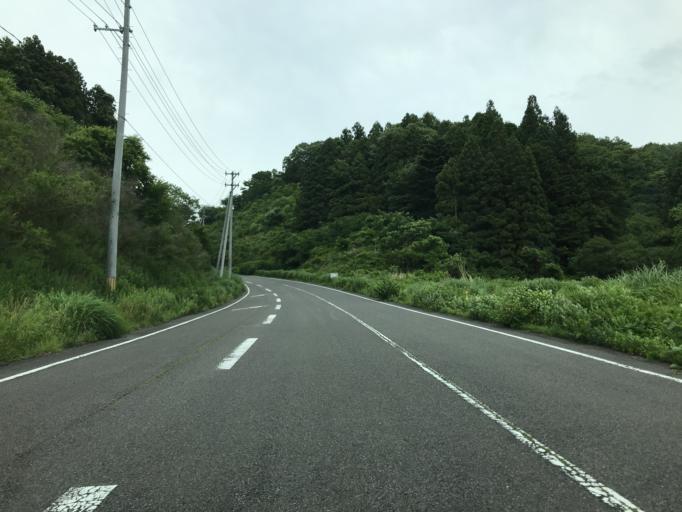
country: JP
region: Fukushima
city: Funehikimachi-funehiki
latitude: 37.4061
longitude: 140.6453
